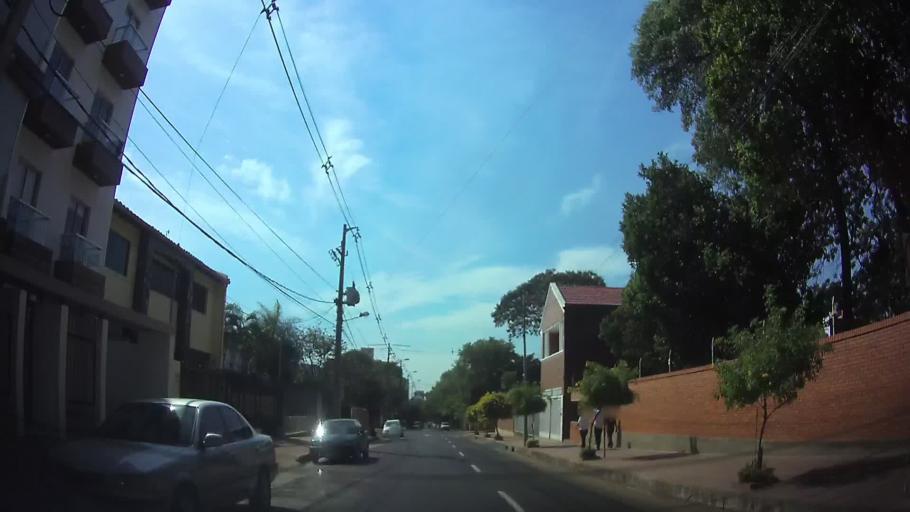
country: PY
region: Asuncion
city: Asuncion
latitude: -25.2918
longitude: -57.6070
